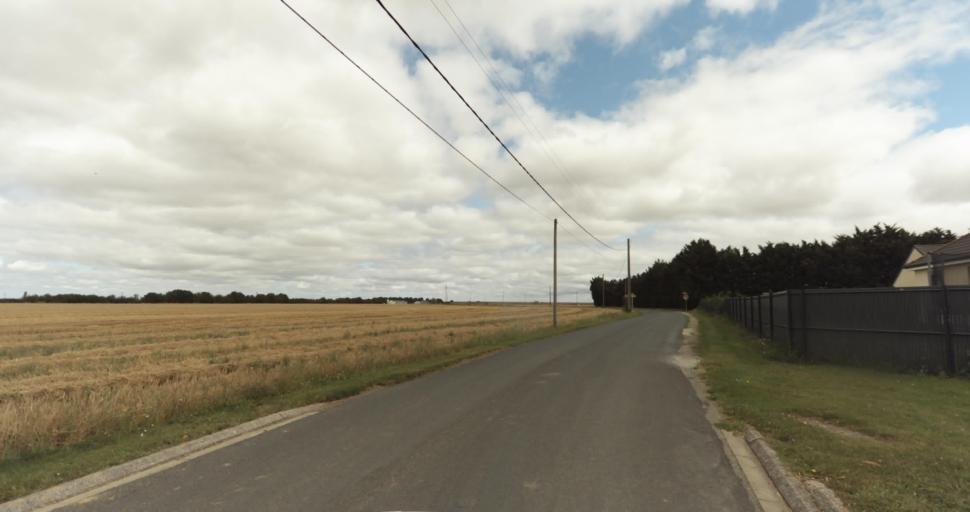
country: FR
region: Haute-Normandie
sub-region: Departement de l'Eure
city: Evreux
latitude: 48.9428
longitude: 1.1969
